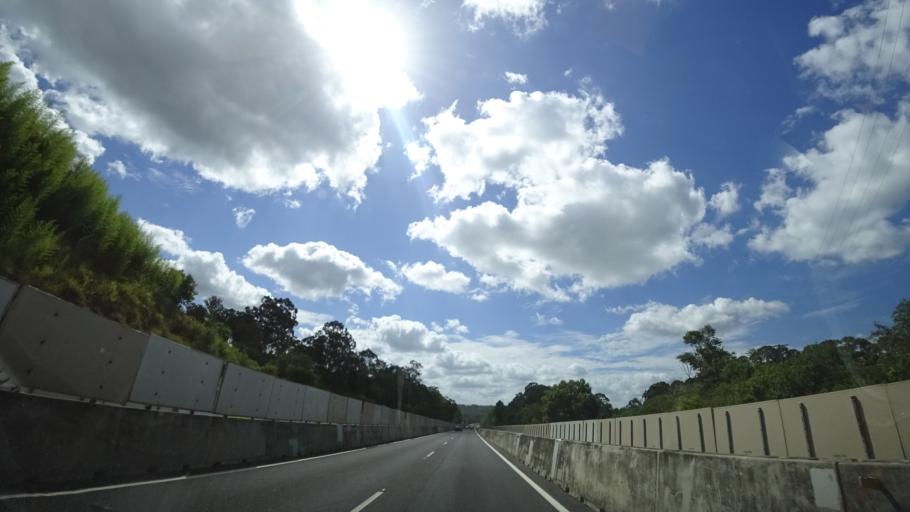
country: AU
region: Queensland
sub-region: Sunshine Coast
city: Buderim
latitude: -26.7189
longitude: 153.0376
